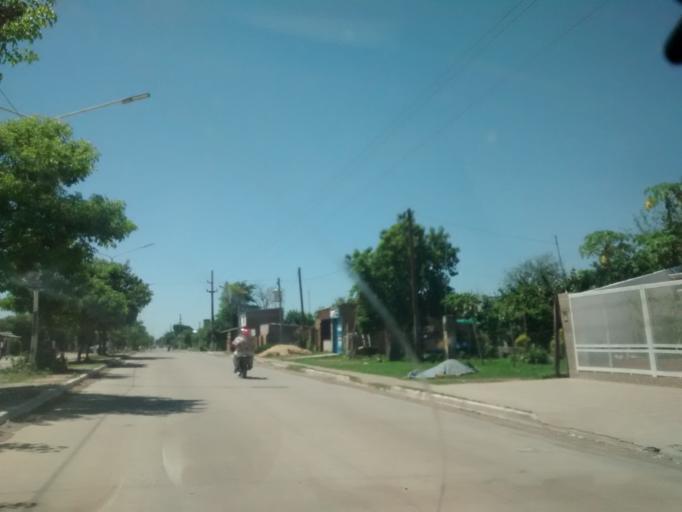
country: AR
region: Chaco
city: Fontana
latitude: -27.4197
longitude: -59.0220
